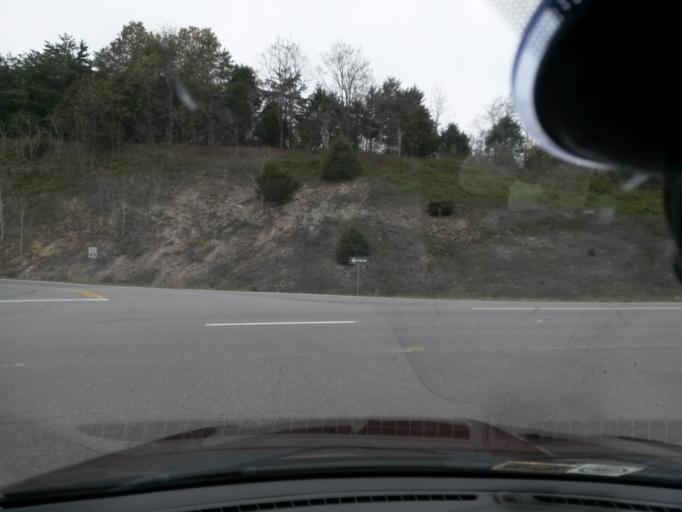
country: US
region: Virginia
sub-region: Botetourt County
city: Fincastle
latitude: 37.6076
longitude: -79.8341
